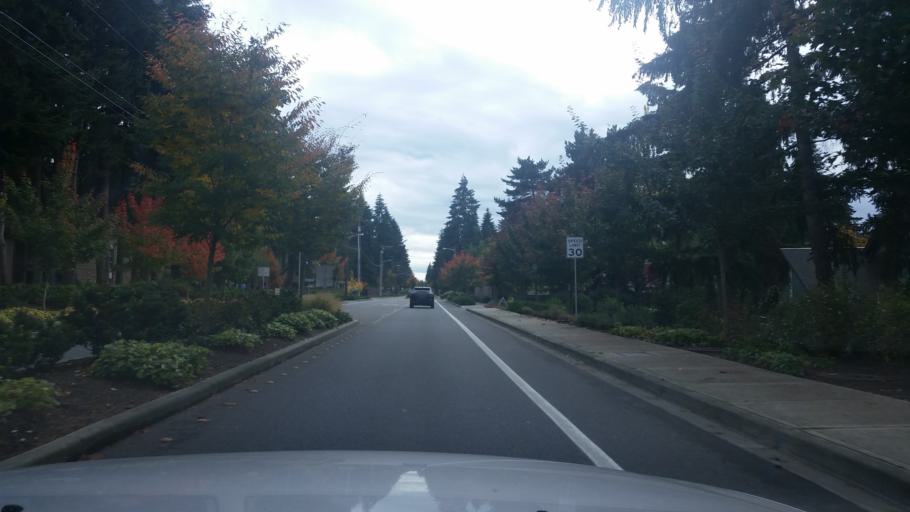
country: US
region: Washington
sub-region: King County
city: Eastgate
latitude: 47.5953
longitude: -122.1495
